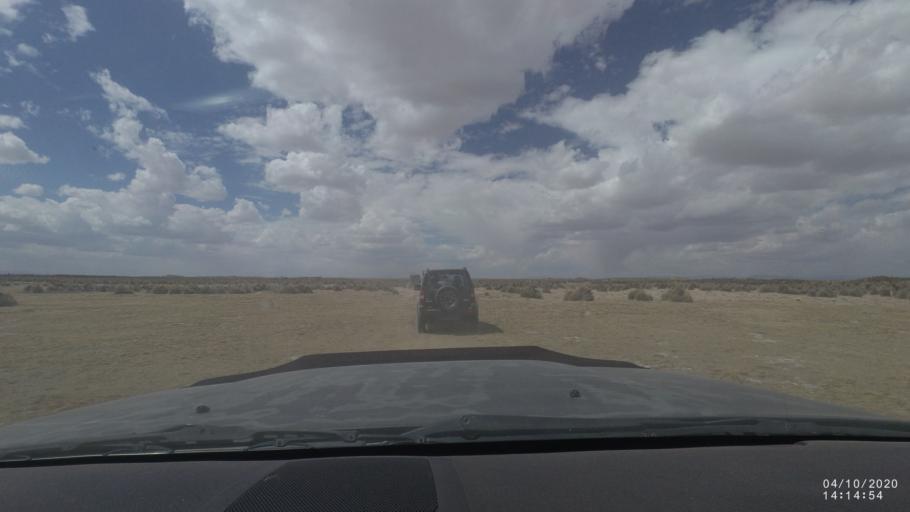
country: BO
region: Oruro
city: Poopo
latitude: -18.6941
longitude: -67.4543
